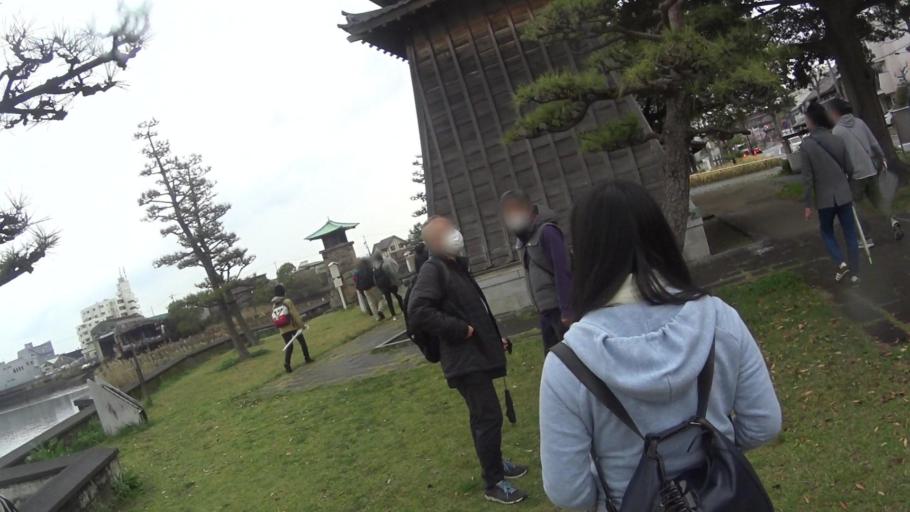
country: JP
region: Aichi
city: Nagoya-shi
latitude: 35.1188
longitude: 136.9053
